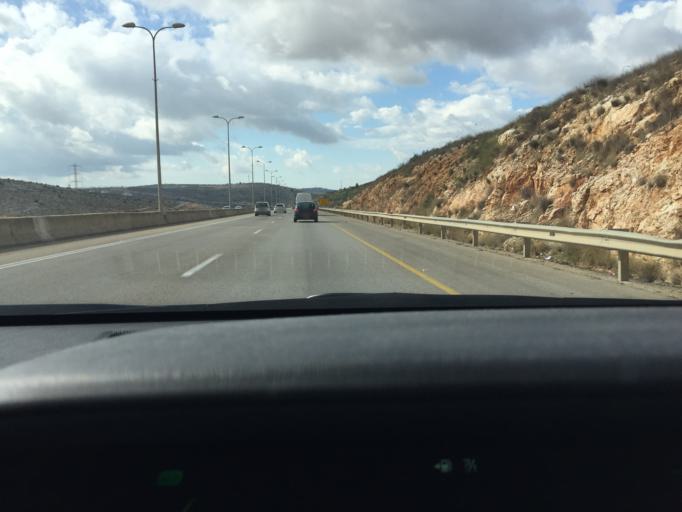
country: IL
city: Revava
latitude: 32.0992
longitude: 35.1191
